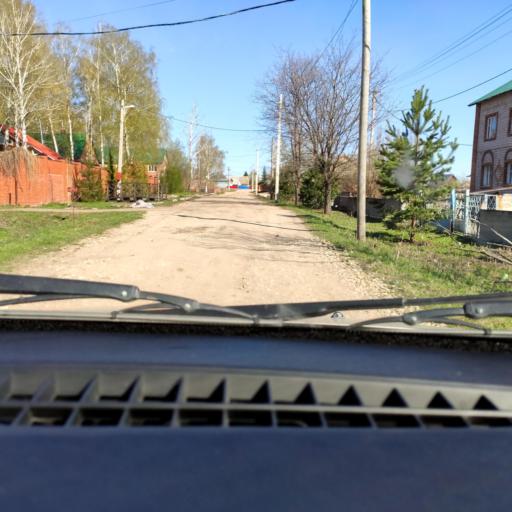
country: RU
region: Bashkortostan
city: Kabakovo
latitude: 54.5939
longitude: 56.1747
